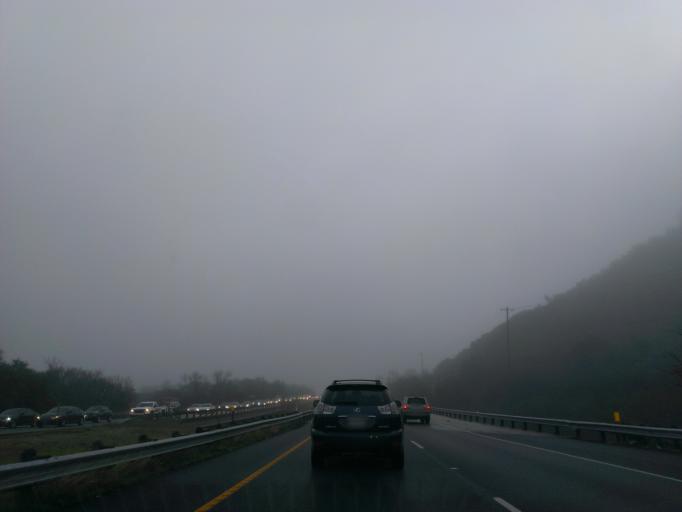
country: US
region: Texas
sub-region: Williamson County
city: Jollyville
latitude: 30.3717
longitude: -97.7854
